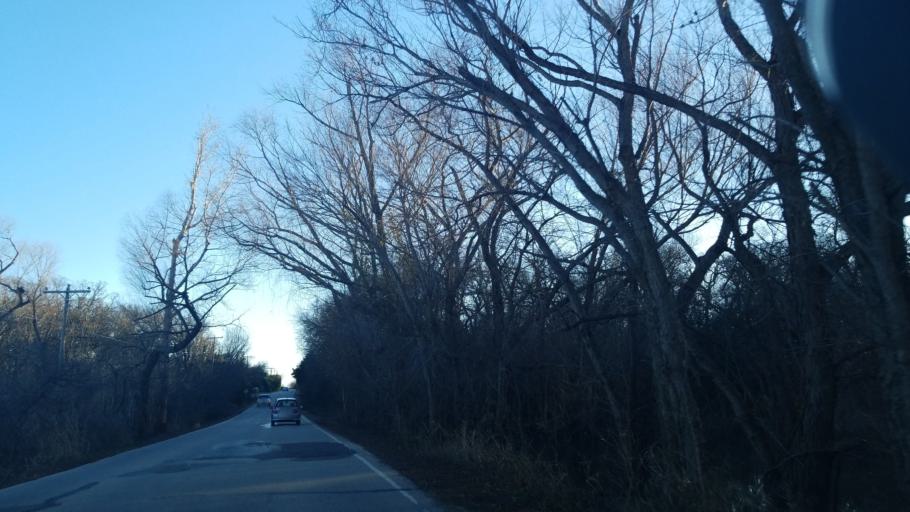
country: US
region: Texas
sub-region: Denton County
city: Shady Shores
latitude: 33.1483
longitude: -97.0299
